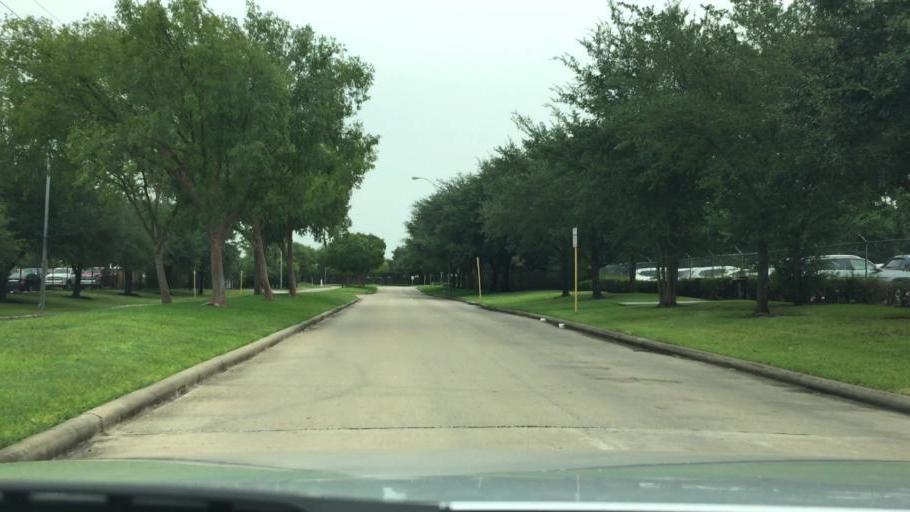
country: US
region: Texas
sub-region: Harris County
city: Oak Cliff Place
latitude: 29.9115
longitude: -95.6106
